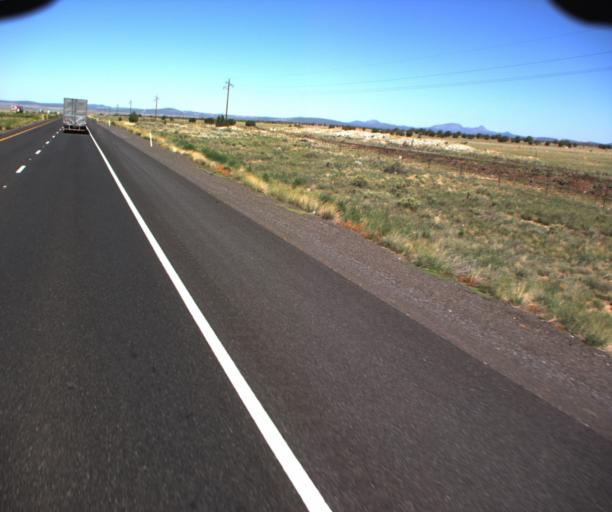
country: US
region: Arizona
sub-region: Yavapai County
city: Paulden
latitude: 35.2225
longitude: -112.5493
